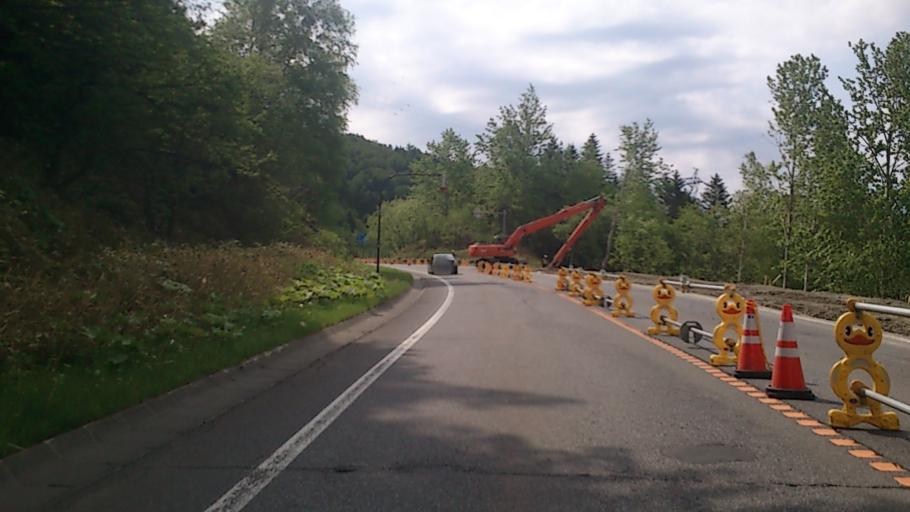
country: JP
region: Hokkaido
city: Kamikawa
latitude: 43.6842
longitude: 143.0328
